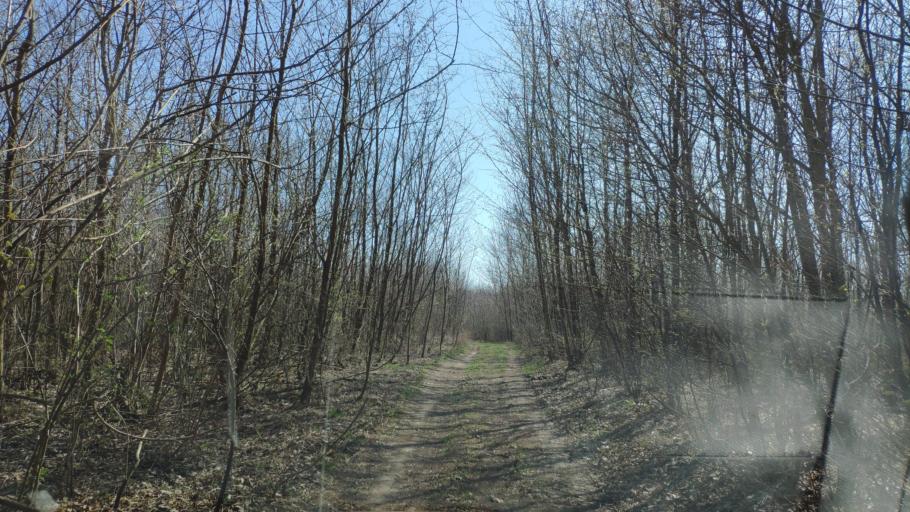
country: SK
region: Kosicky
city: Moldava nad Bodvou
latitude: 48.5624
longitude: 20.9319
